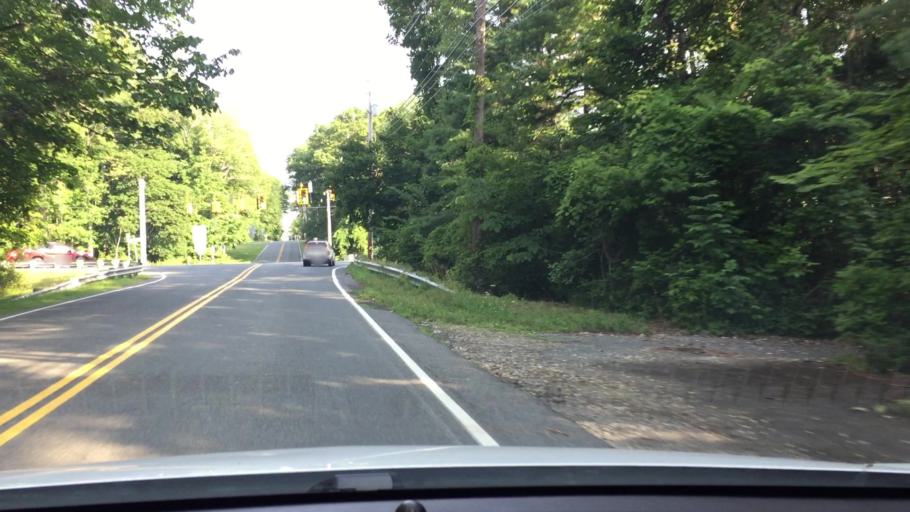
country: US
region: Massachusetts
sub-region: Berkshire County
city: Lenox
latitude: 42.3472
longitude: -73.2685
